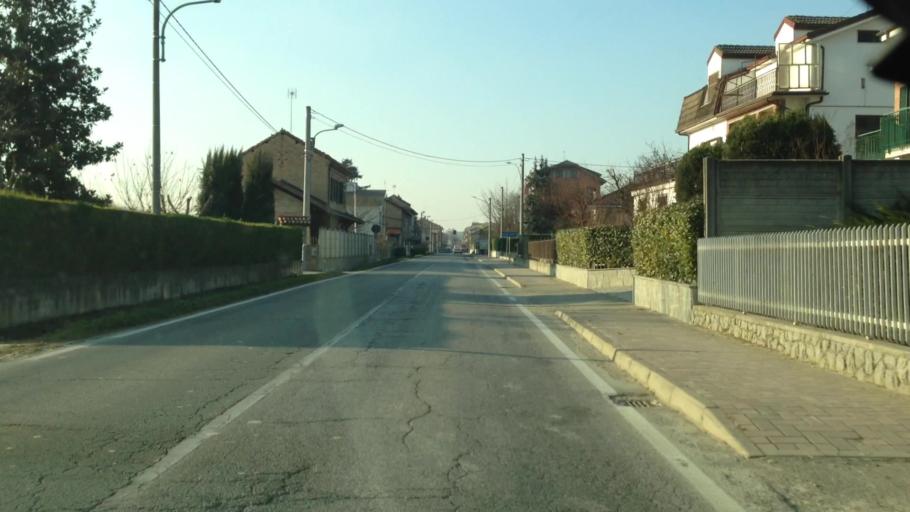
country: IT
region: Piedmont
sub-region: Provincia di Asti
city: Montegrosso
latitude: 44.8173
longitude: 8.2479
